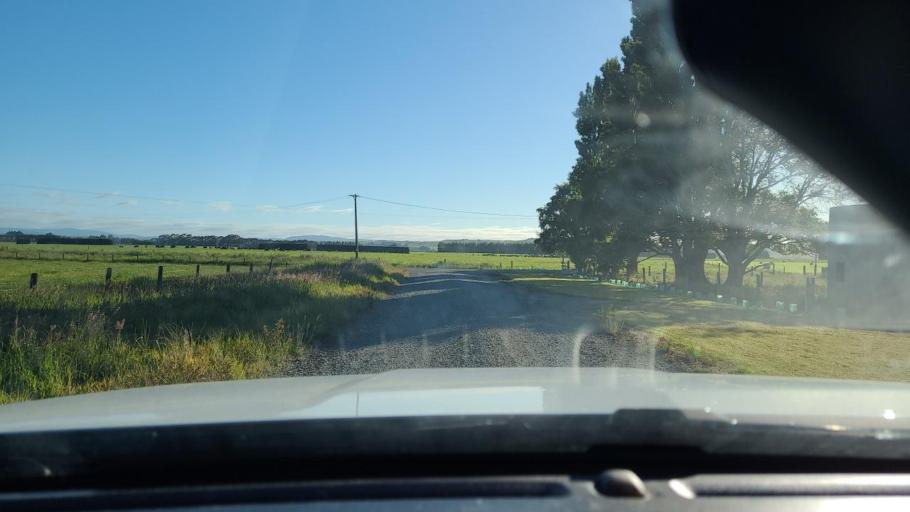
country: NZ
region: Southland
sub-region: Southland District
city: Winton
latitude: -46.1937
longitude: 168.3504
